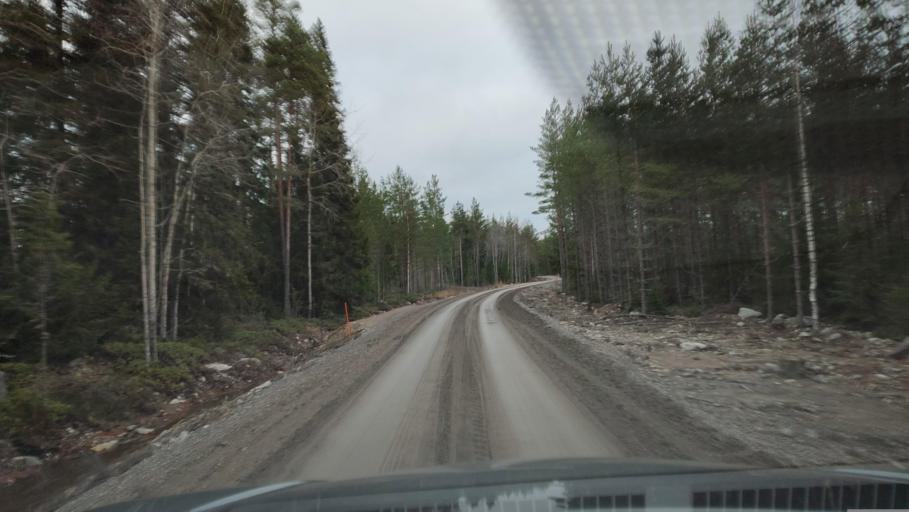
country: FI
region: Southern Ostrobothnia
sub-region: Suupohja
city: Karijoki
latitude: 62.1961
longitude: 21.5891
